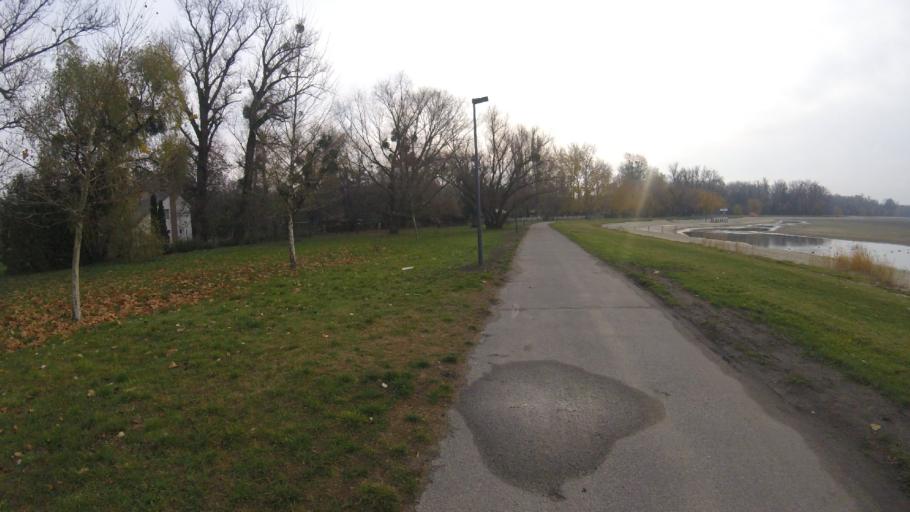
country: HU
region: Komarom-Esztergom
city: Tata
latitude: 47.6433
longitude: 18.3357
